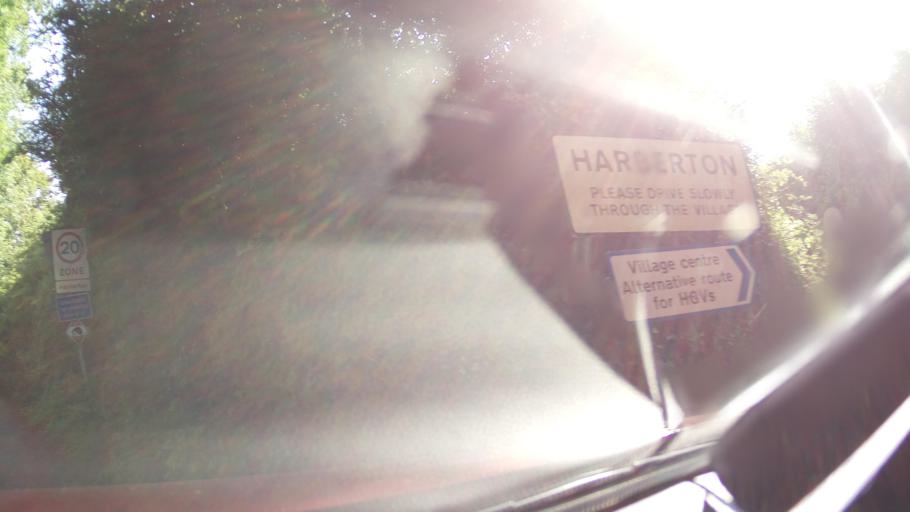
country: GB
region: England
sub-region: Devon
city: Totnes
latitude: 50.4176
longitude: -3.7217
